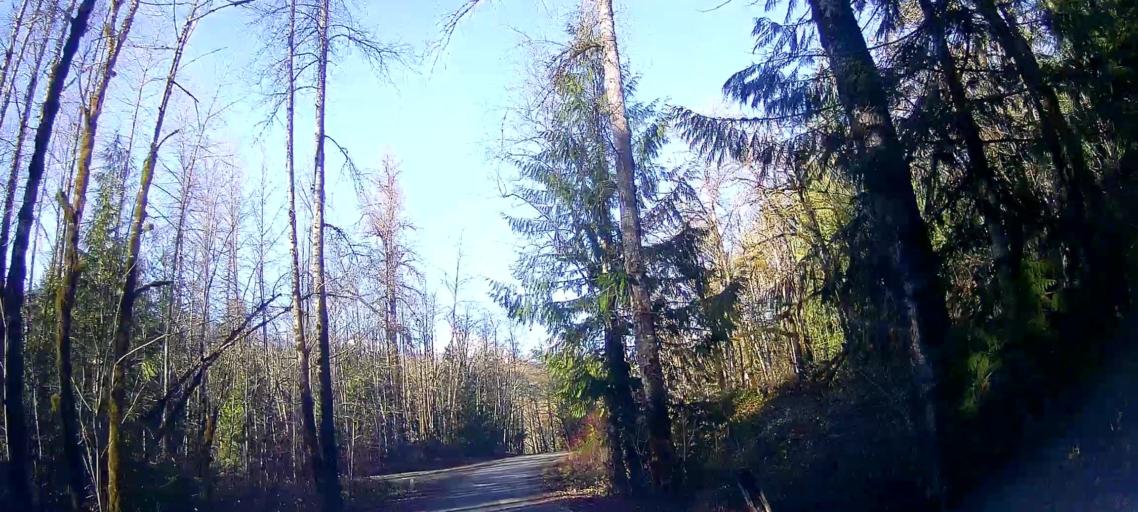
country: US
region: Washington
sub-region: Snohomish County
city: Darrington
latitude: 48.5465
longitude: -121.7392
